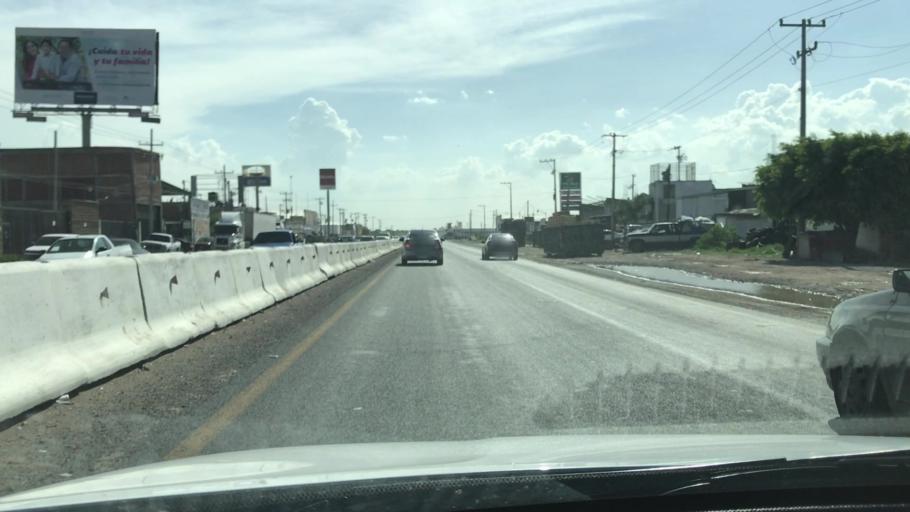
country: MX
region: Guanajuato
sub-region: Celaya
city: Colonia Pedro Maria Anaya
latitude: 20.5179
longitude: -100.8602
